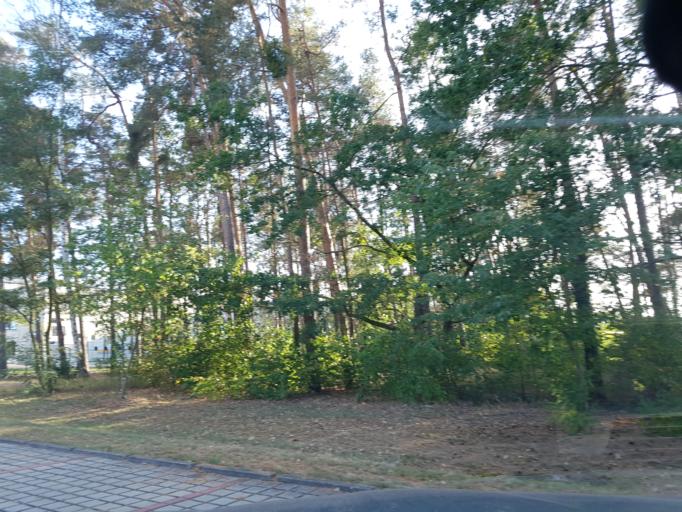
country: DE
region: Brandenburg
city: Bad Liebenwerda
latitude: 51.5290
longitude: 13.4006
